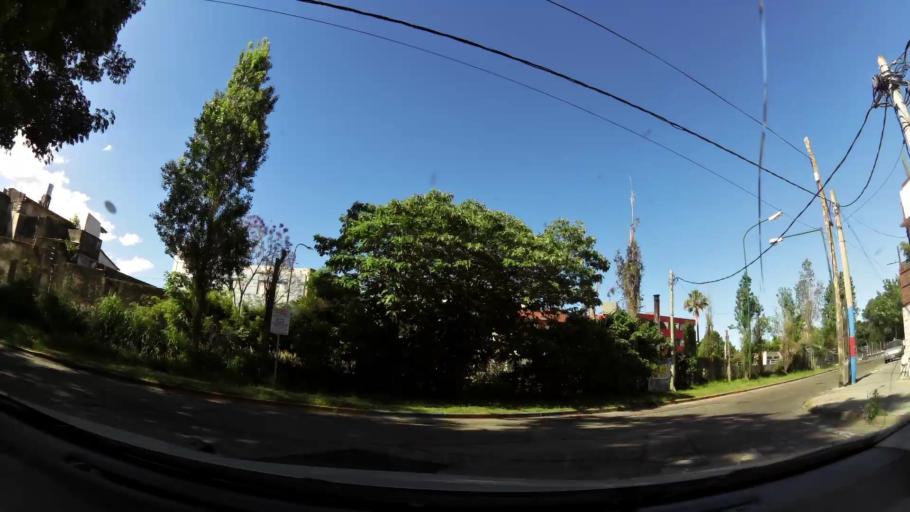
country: AR
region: Buenos Aires
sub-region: Partido de San Isidro
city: San Isidro
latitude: -34.4572
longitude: -58.5343
